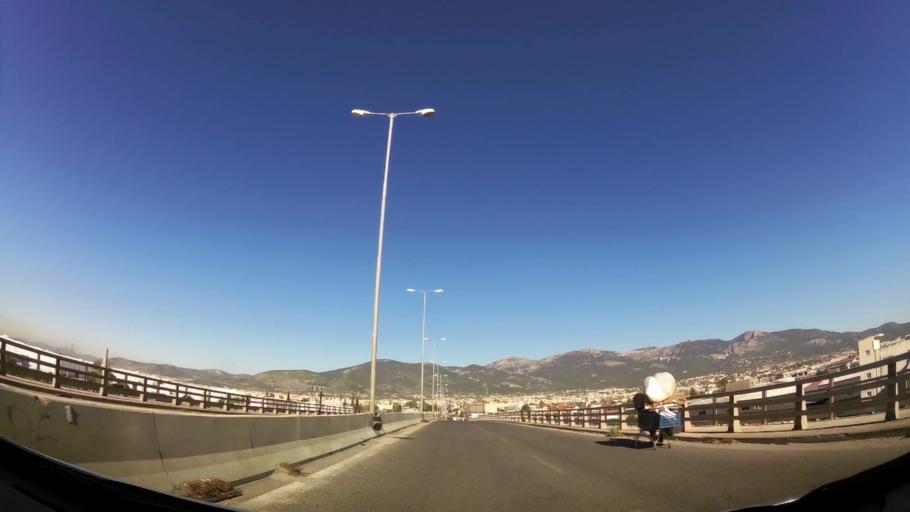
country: GR
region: Attica
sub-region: Nomarchia Athinas
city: Metamorfosi
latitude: 38.0876
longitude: 23.7616
